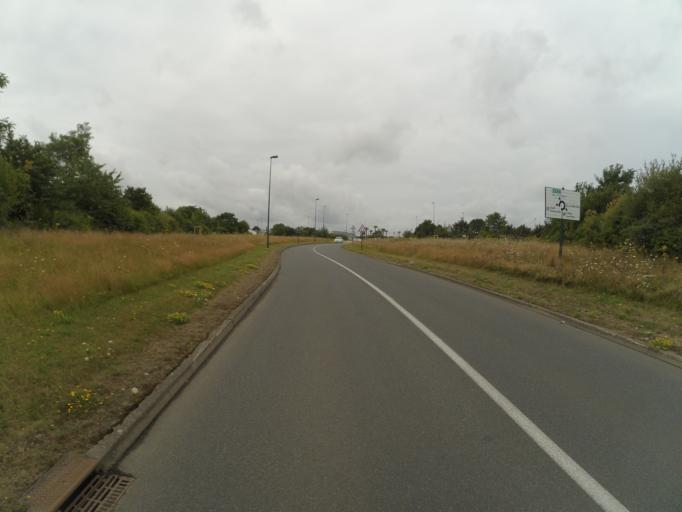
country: FR
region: Brittany
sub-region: Departement des Cotes-d'Armor
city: Ploufragan
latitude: 48.5148
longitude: -2.7929
